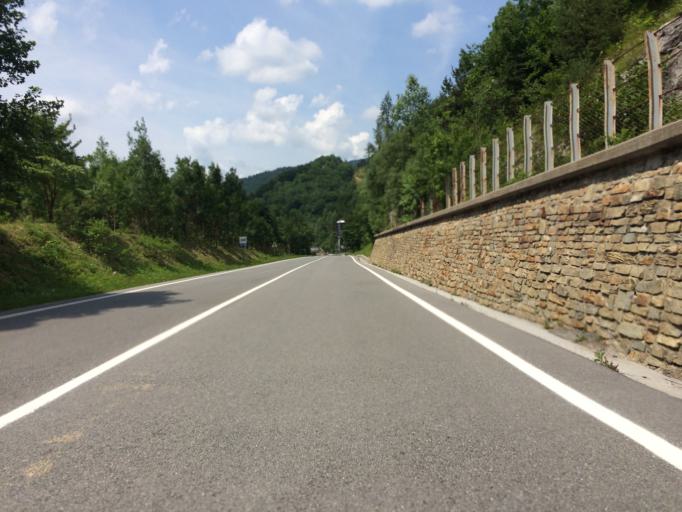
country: IT
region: Piedmont
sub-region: Provincia di Cuneo
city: Limone Piemonte
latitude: 44.2194
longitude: 7.5692
